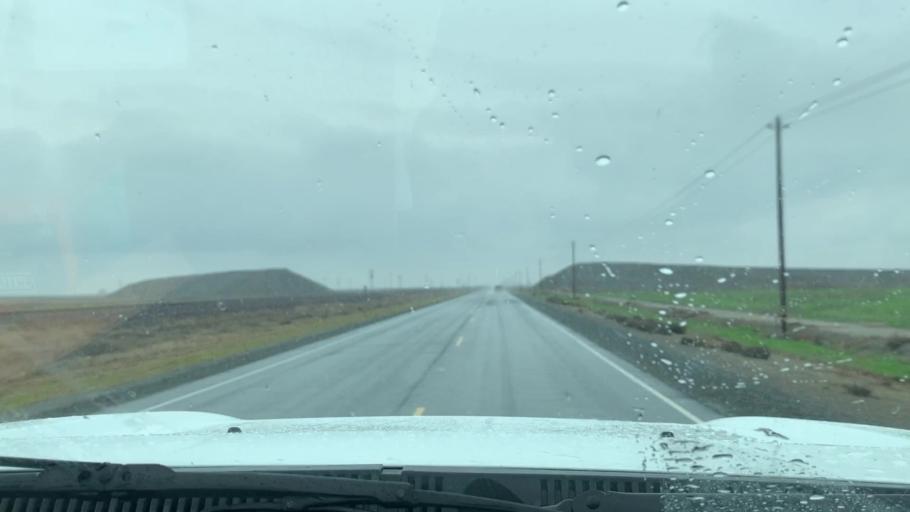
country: US
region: California
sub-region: Tulare County
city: Alpaugh
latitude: 35.9450
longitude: -119.4444
